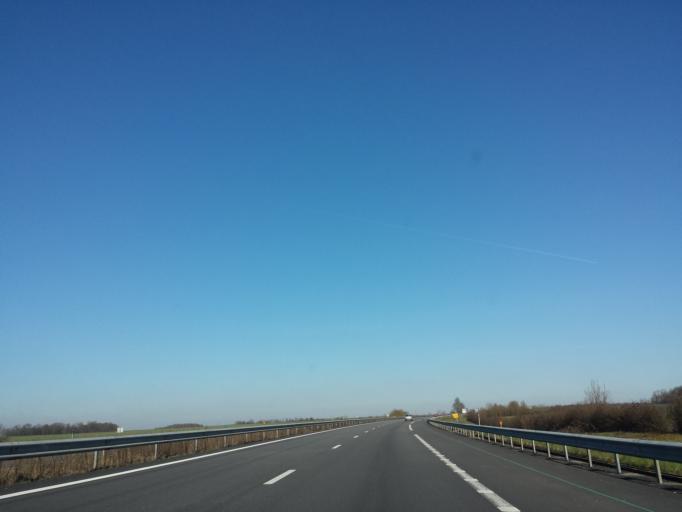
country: FR
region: Picardie
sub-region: Departement de l'Oise
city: Saint-Crepin-Ibouvillers
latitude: 49.2869
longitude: 2.0735
